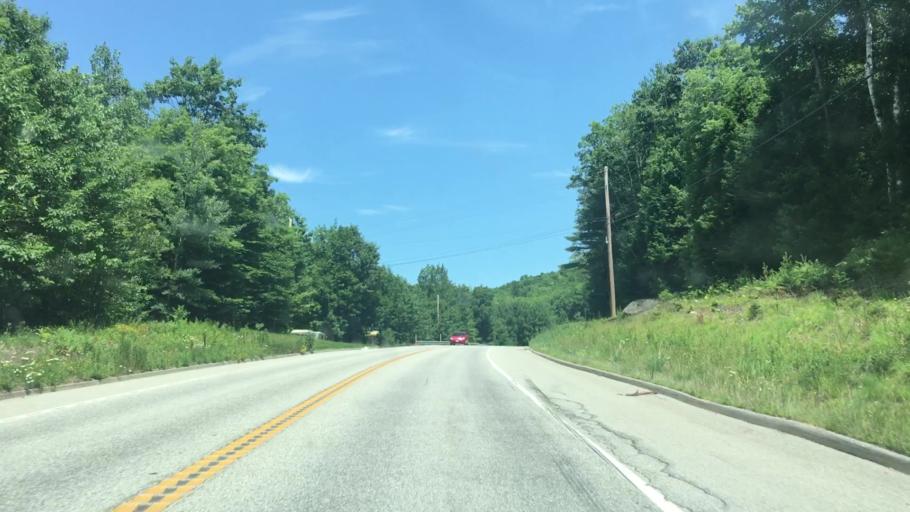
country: US
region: Maine
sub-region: Androscoggin County
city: Livermore
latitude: 44.4113
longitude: -70.2226
